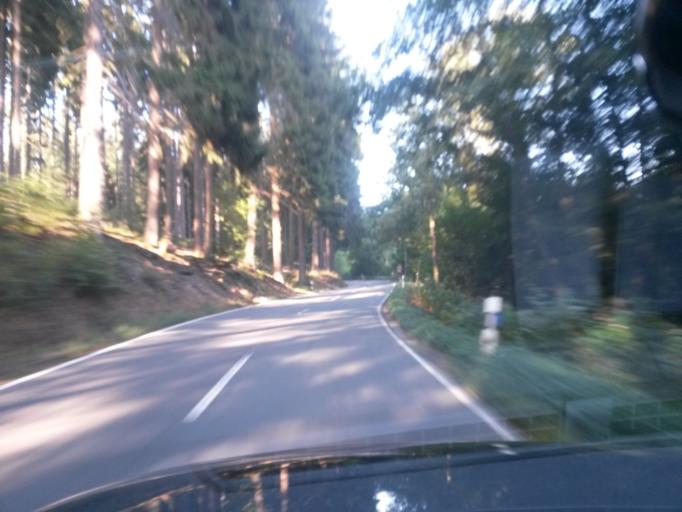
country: DE
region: North Rhine-Westphalia
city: Wiehl
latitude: 50.9648
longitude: 7.5749
